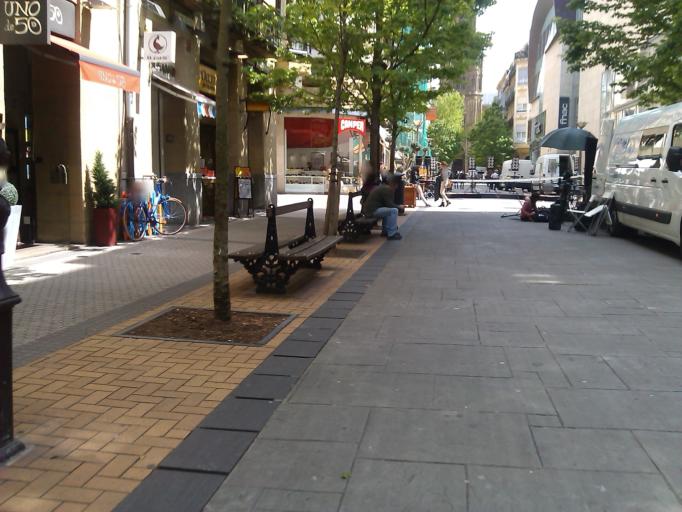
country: ES
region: Basque Country
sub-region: Provincia de Guipuzcoa
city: San Sebastian
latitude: 43.3188
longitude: -1.9831
